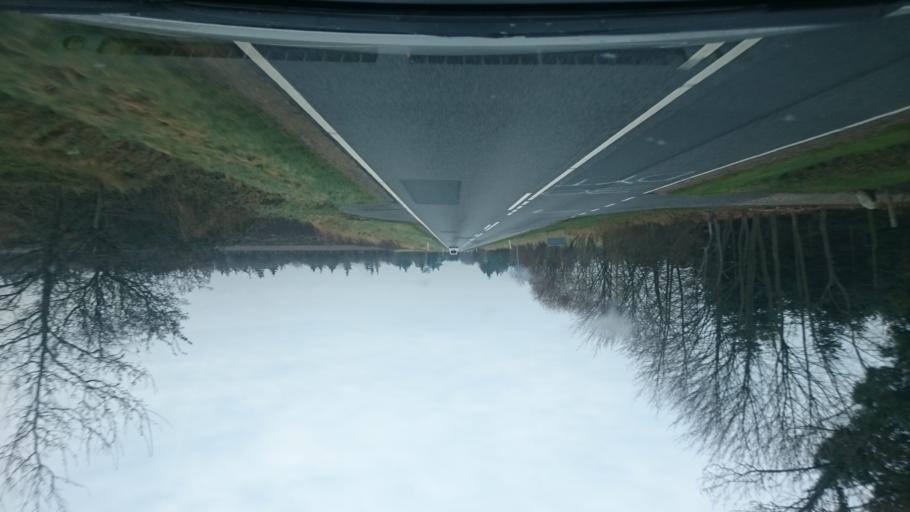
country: DK
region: South Denmark
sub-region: Esbjerg Kommune
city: Ribe
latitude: 55.3326
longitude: 8.8882
